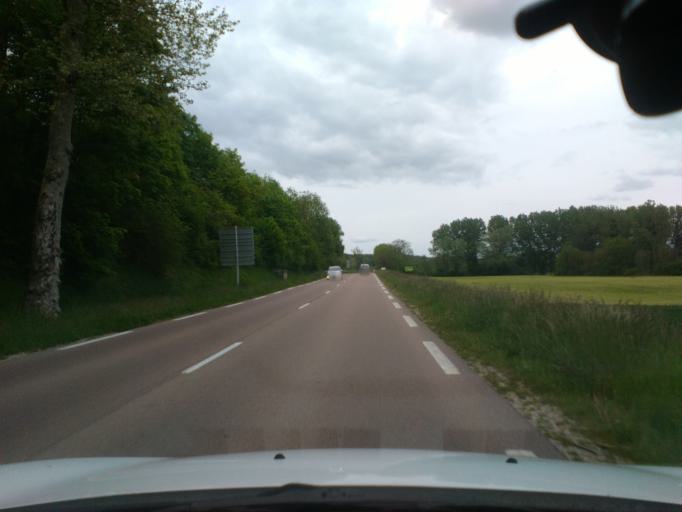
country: FR
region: Champagne-Ardenne
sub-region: Departement de l'Aube
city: Bar-sur-Aube
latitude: 48.2720
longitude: 4.6297
